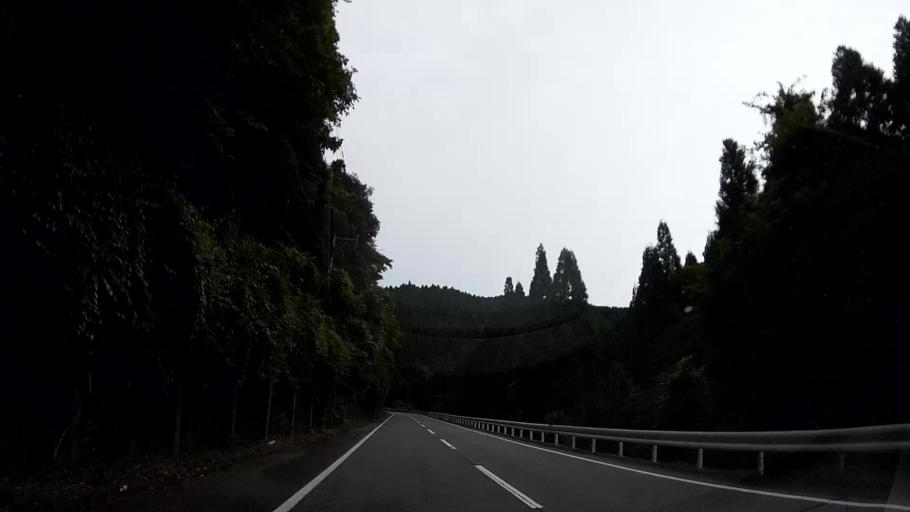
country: JP
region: Kumamoto
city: Kikuchi
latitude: 33.0460
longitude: 130.8962
